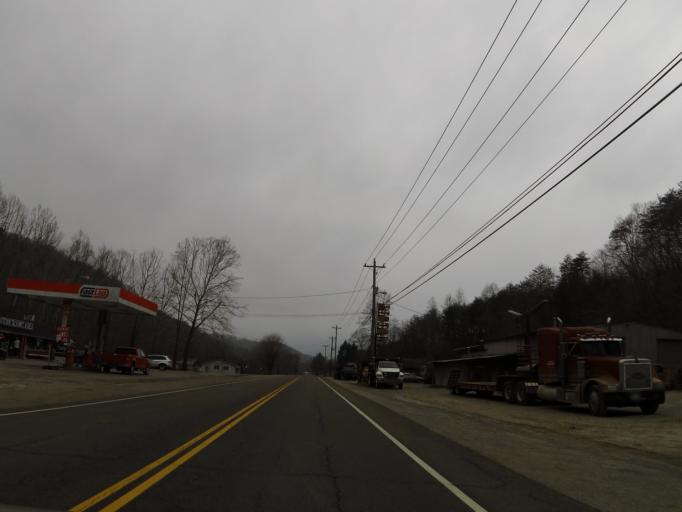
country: US
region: Tennessee
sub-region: Anderson County
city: Clinton
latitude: 36.1482
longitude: -84.1498
